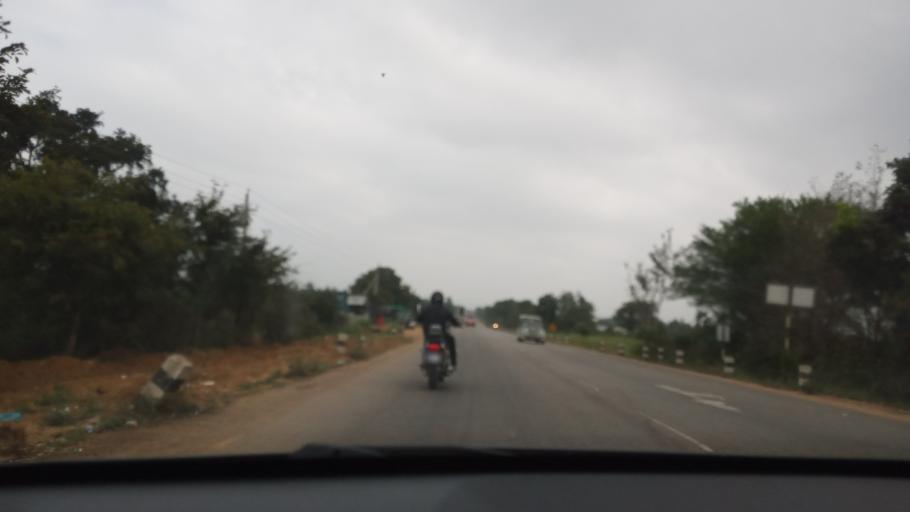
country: IN
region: Karnataka
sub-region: Bangalore Rural
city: Vijayapura
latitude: 13.2514
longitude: 77.9383
